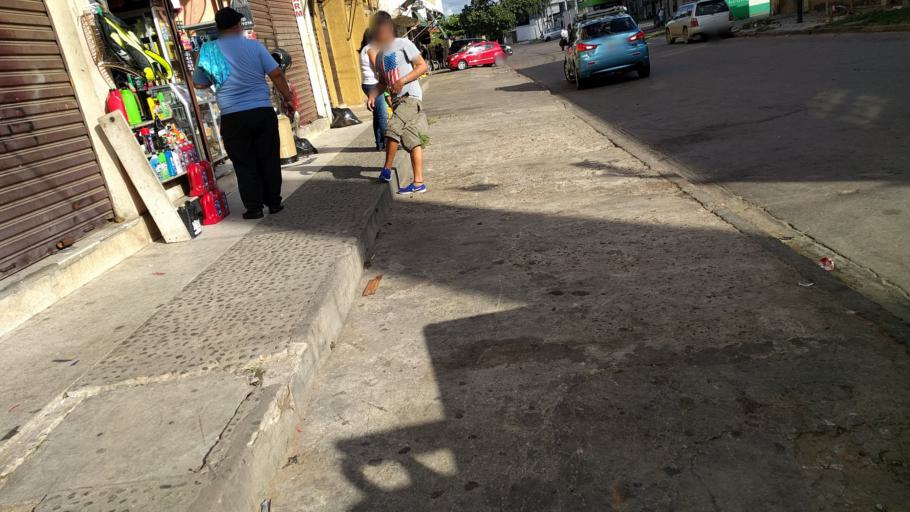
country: BO
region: Santa Cruz
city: Santa Cruz de la Sierra
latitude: -17.7743
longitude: -63.1652
